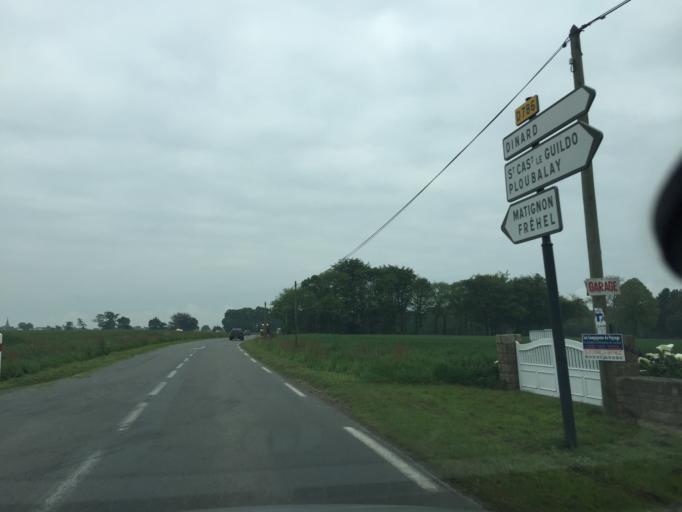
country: FR
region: Brittany
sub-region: Departement des Cotes-d'Armor
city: Matignon
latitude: 48.5955
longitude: -2.2745
